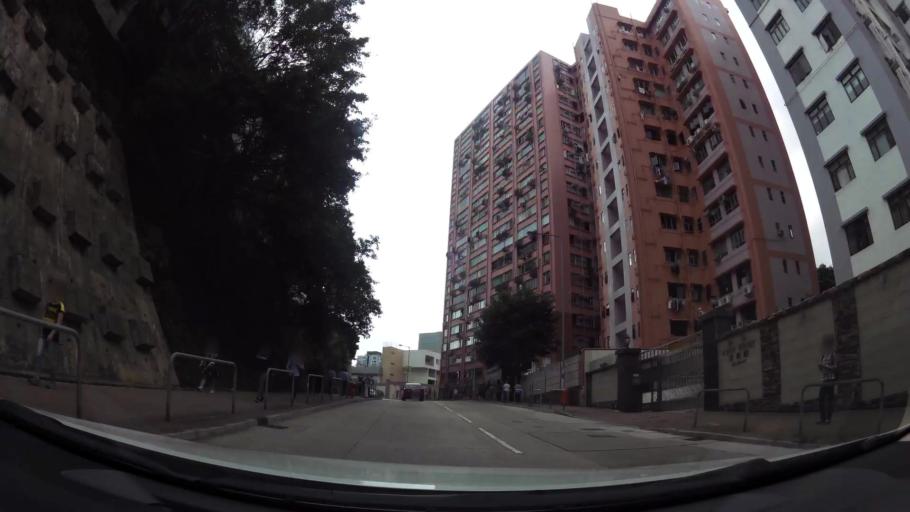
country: HK
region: Kowloon City
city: Kowloon
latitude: 22.3197
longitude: 114.1839
